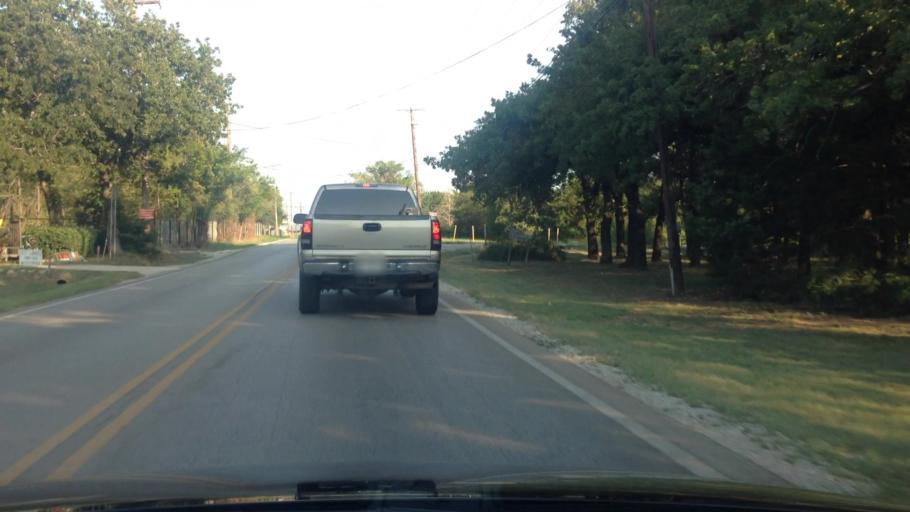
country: US
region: Texas
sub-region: Tarrant County
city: Rendon
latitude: 32.5969
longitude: -97.2592
